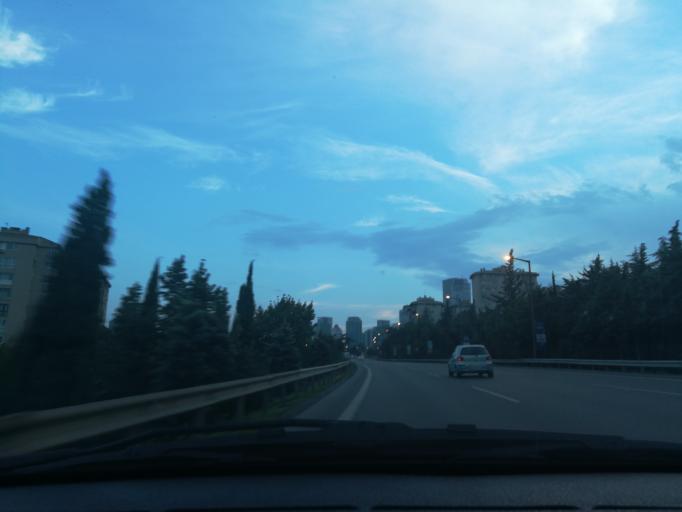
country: TR
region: Istanbul
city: Sisli
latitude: 41.0922
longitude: 29.0207
